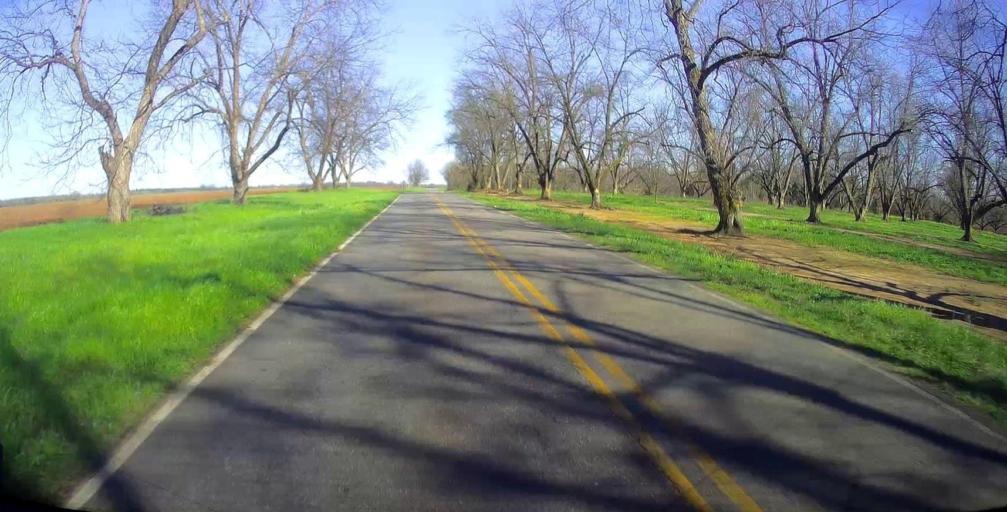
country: US
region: Georgia
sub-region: Peach County
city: Fort Valley
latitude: 32.6443
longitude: -83.8626
